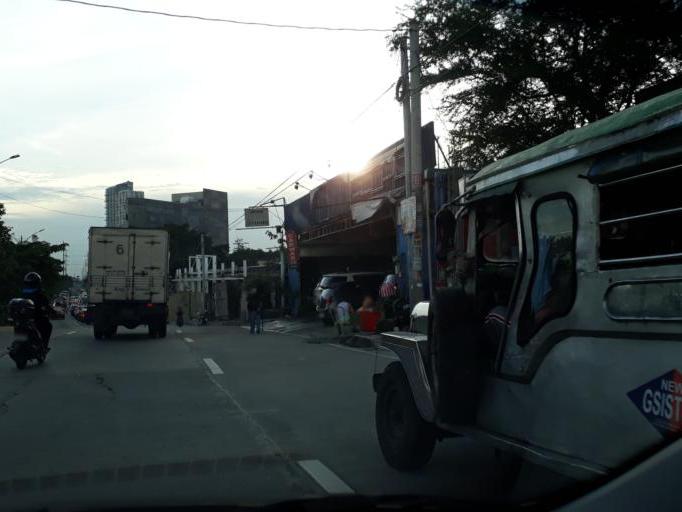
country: PH
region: Calabarzon
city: Bagong Pagasa
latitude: 14.6729
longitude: 121.0471
